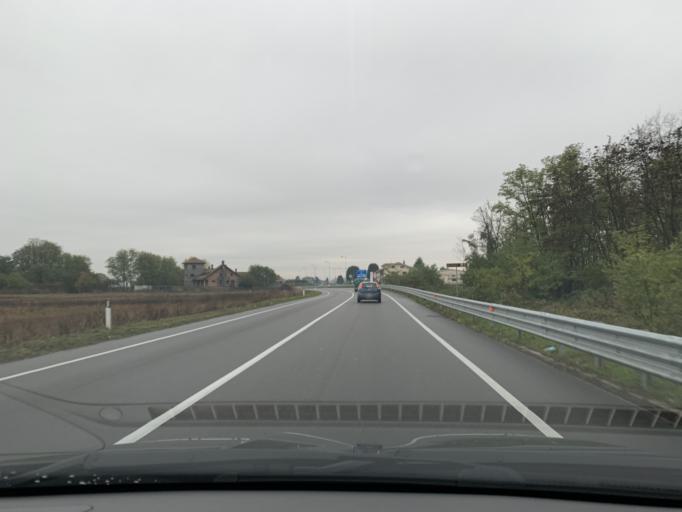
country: IT
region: Lombardy
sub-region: Provincia di Como
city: Rovellasca
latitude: 45.6544
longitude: 9.0523
